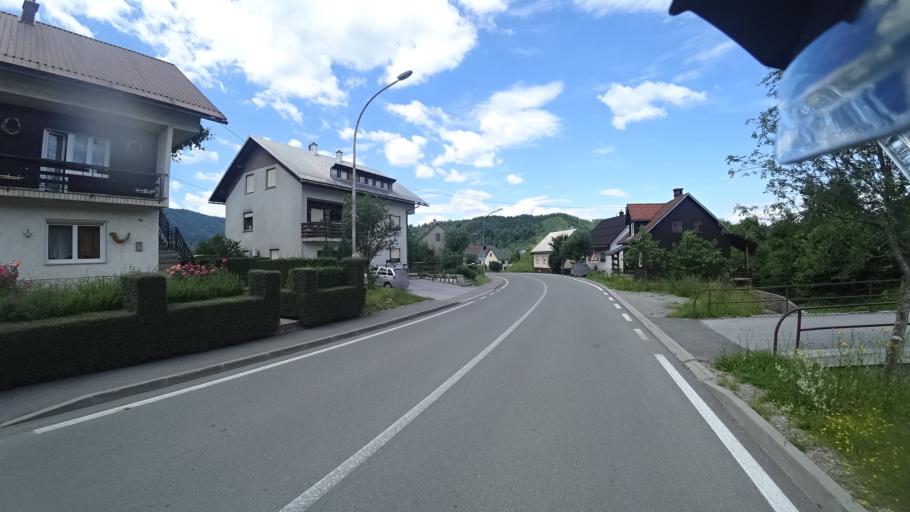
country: SI
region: Osilnica
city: Osilnica
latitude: 45.5112
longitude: 14.6359
